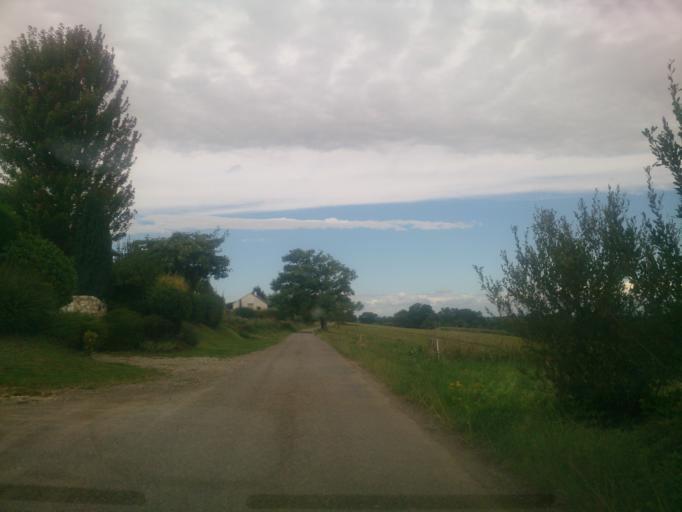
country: FR
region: Midi-Pyrenees
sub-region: Departement des Hautes-Pyrenees
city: Horgues
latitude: 43.1374
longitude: 0.0771
